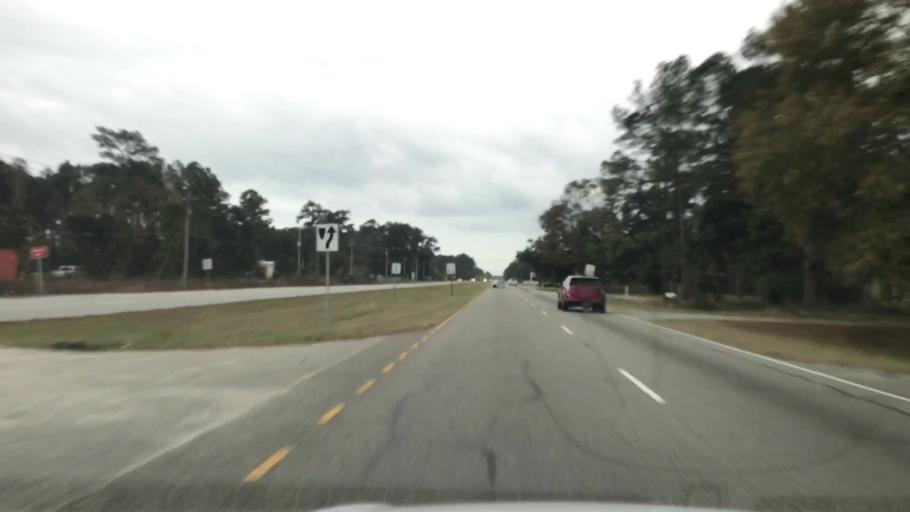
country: US
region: South Carolina
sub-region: Georgetown County
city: Georgetown
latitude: 33.3204
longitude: -79.3224
